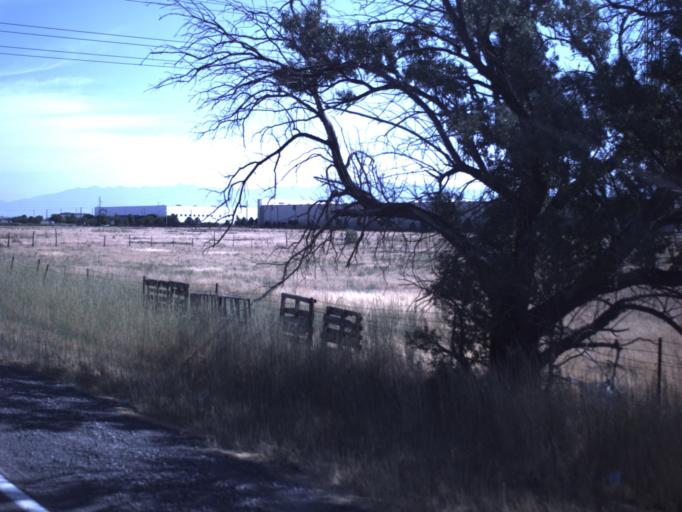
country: US
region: Utah
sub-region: Salt Lake County
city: West Valley City
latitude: 40.7574
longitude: -112.0249
